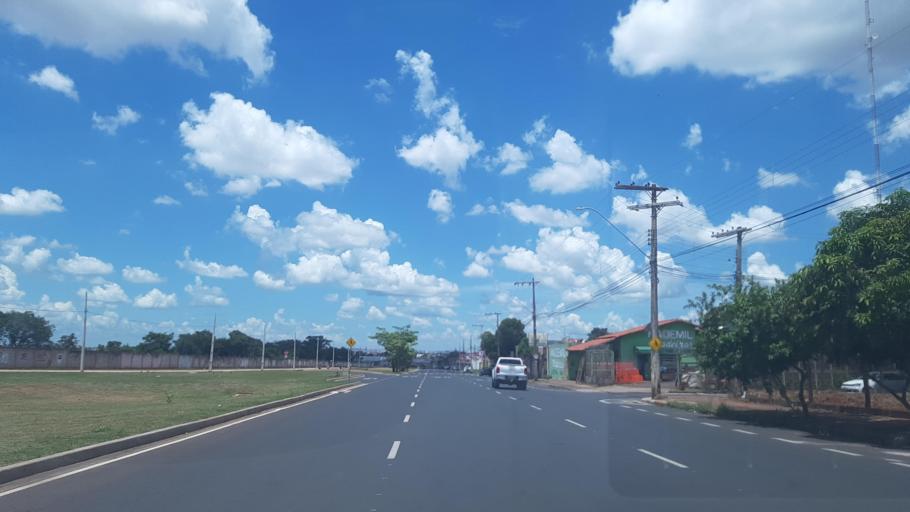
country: BR
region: Minas Gerais
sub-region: Uberlandia
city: Uberlandia
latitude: -18.9575
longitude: -48.3330
